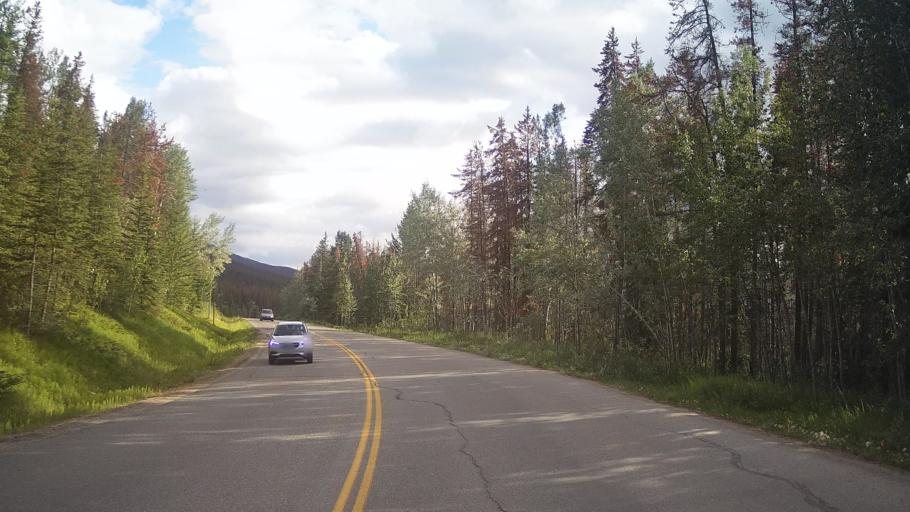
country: CA
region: Alberta
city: Jasper Park Lodge
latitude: 52.9180
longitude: -118.0009
